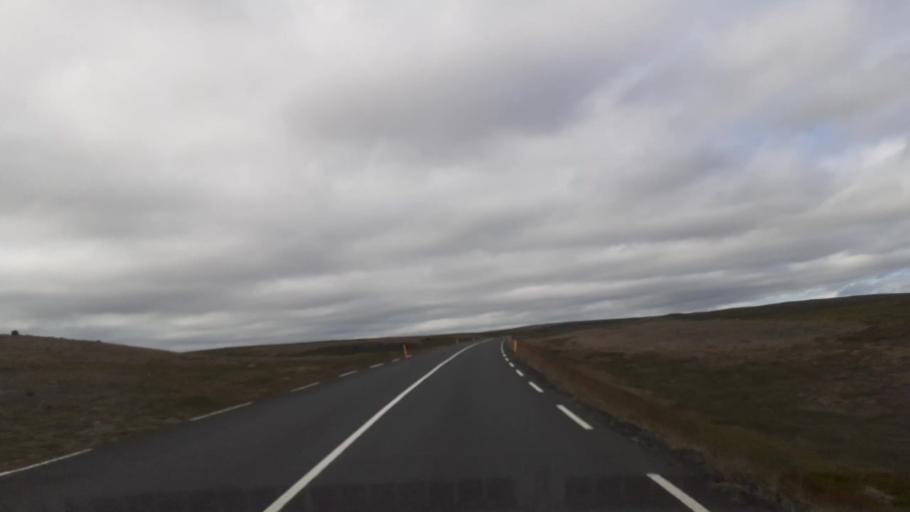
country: IS
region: Northeast
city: Laugar
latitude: 65.6612
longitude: -16.9776
